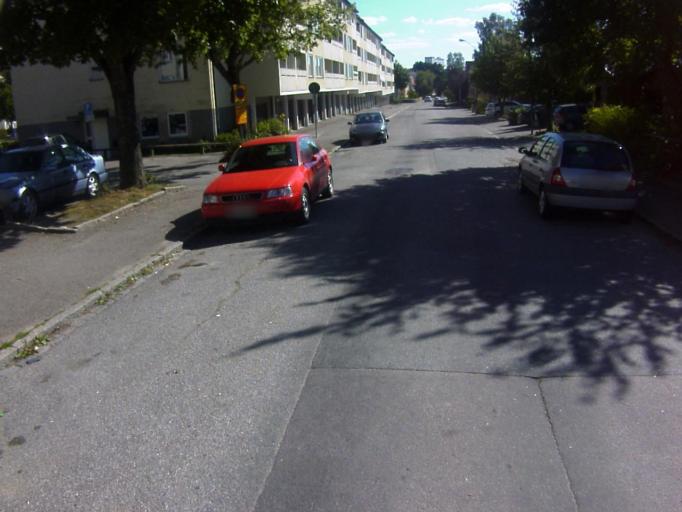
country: SE
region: Soedermanland
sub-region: Eskilstuna Kommun
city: Eskilstuna
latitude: 59.3728
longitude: 16.5309
